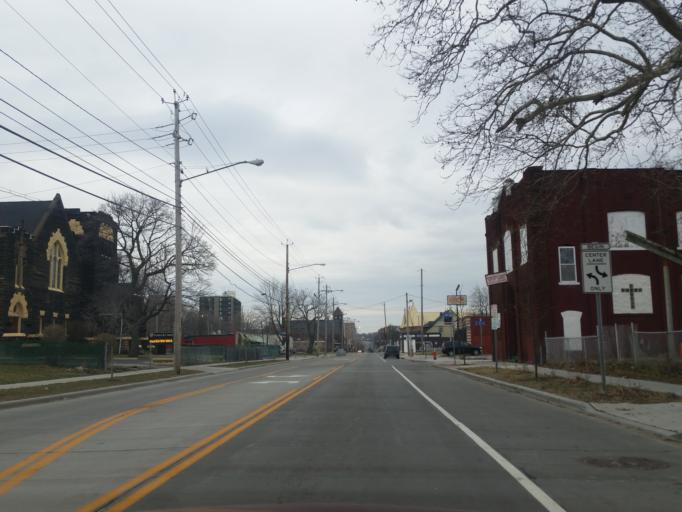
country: US
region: Ohio
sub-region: Cuyahoga County
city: Bratenahl
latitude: 41.4999
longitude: -81.6292
